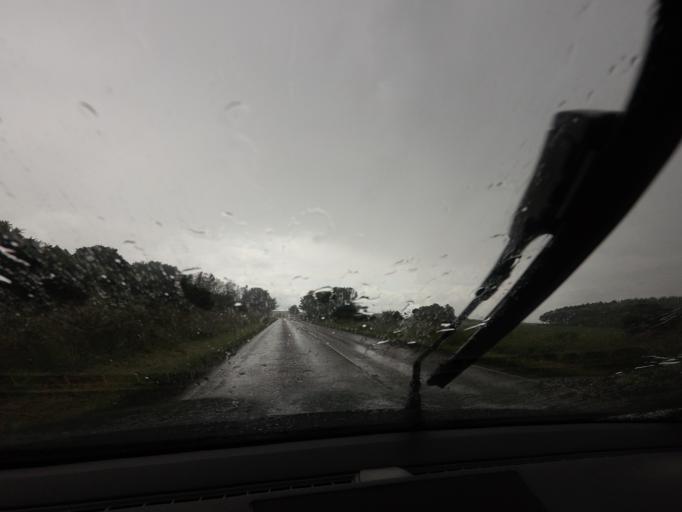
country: GB
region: Scotland
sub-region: Moray
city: Buckie
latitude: 57.6438
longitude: -3.0249
